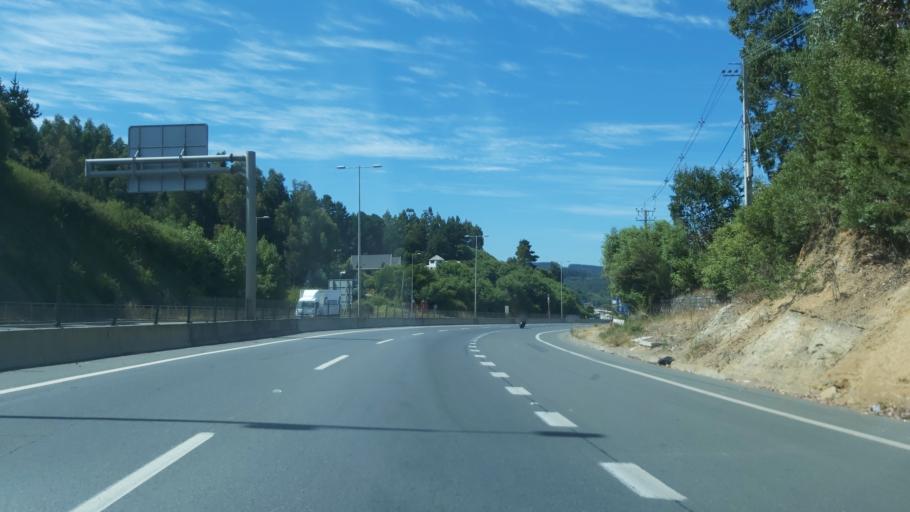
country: CL
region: Biobio
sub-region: Provincia de Concepcion
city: Coronel
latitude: -37.0503
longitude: -73.1411
